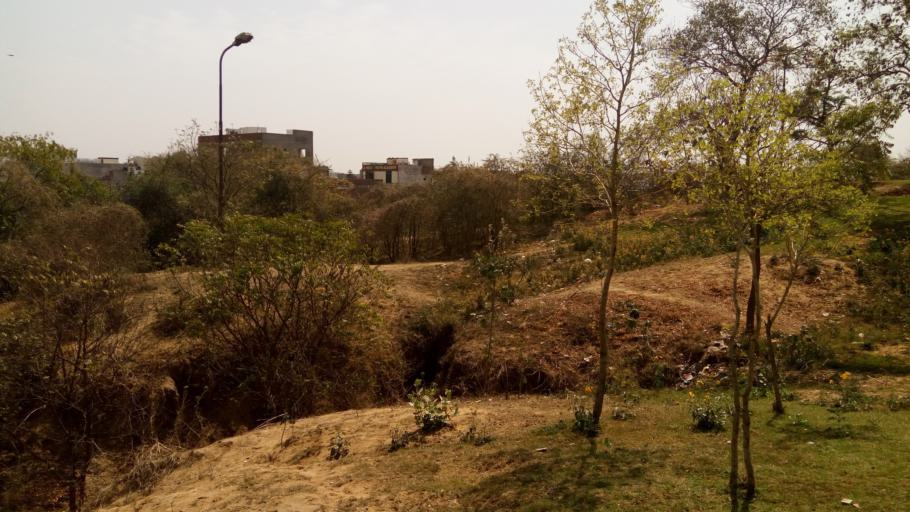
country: IN
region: Rajasthan
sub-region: Jaipur
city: Jaipur
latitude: 26.8625
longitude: 75.7742
